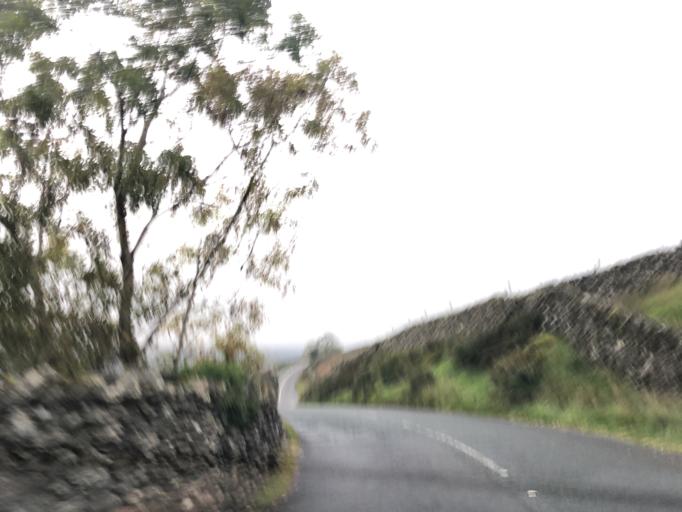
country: GB
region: England
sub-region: Cumbria
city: Ambleside
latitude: 54.4483
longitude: -2.9066
